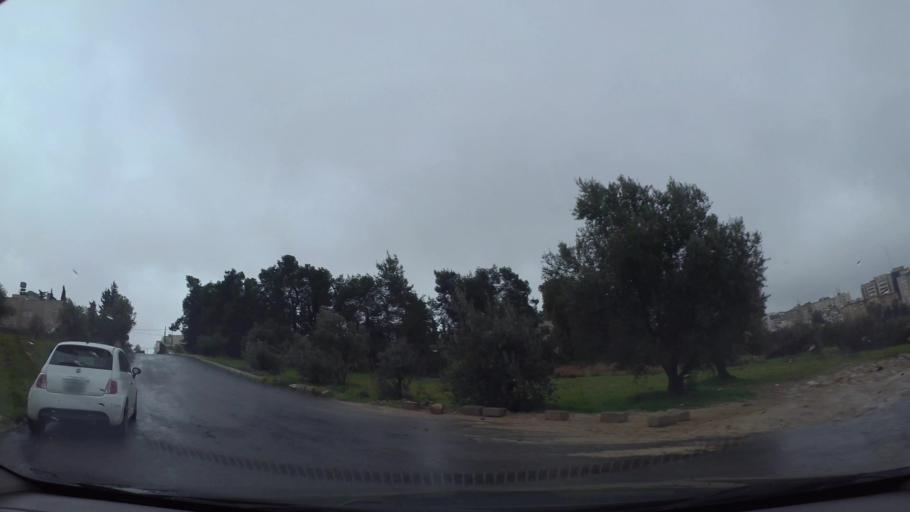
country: JO
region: Amman
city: Al Jubayhah
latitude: 32.0272
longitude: 35.8618
